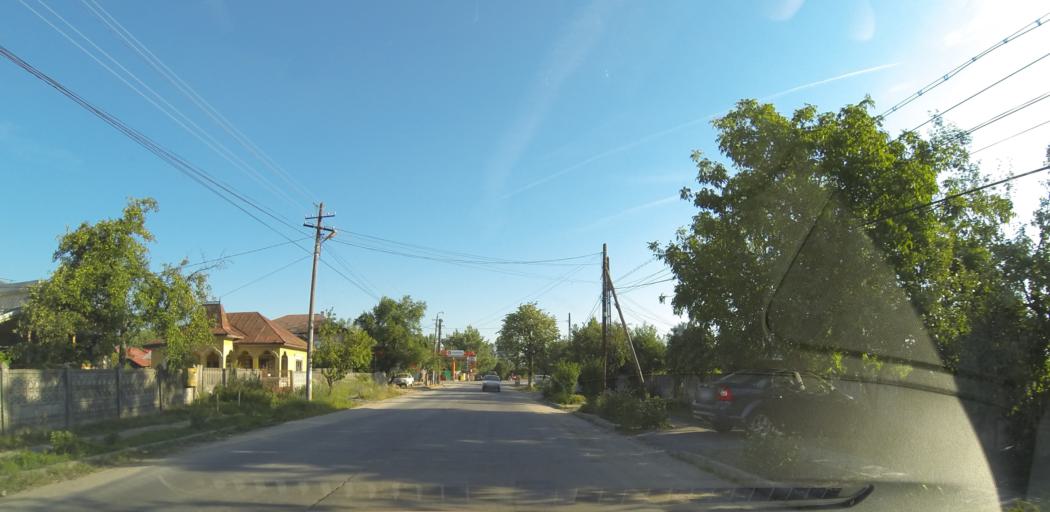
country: RO
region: Valcea
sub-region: Comuna Balcesti
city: Balcesti
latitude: 44.6275
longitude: 23.9412
